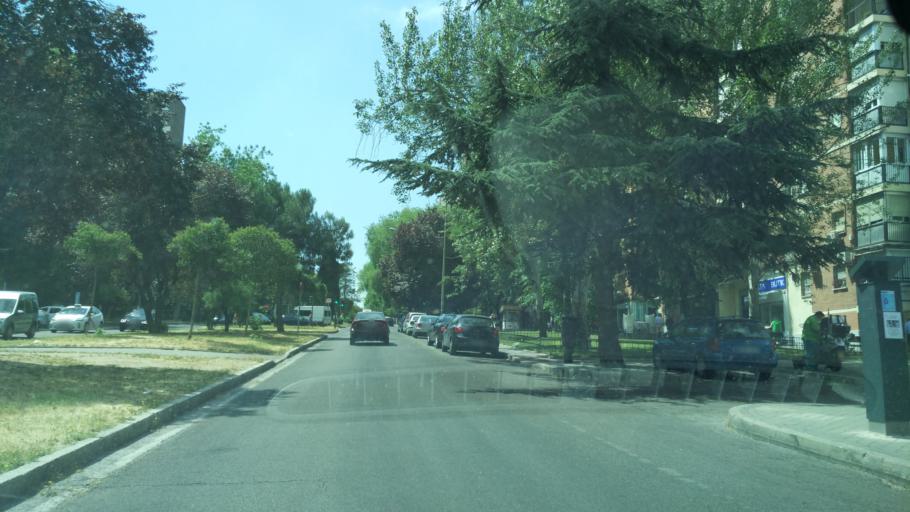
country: ES
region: Madrid
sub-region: Provincia de Madrid
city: Tetuan de las Victorias
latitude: 40.4778
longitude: -3.7037
